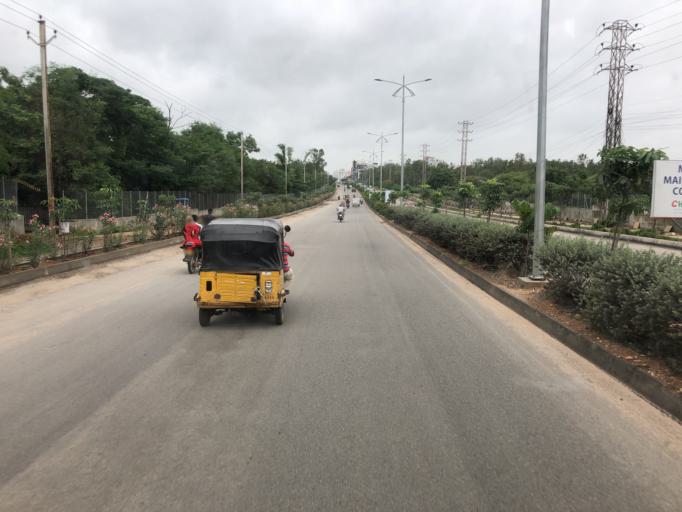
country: IN
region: Telangana
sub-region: Rangareddi
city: Kukatpalli
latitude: 17.4573
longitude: 78.3601
